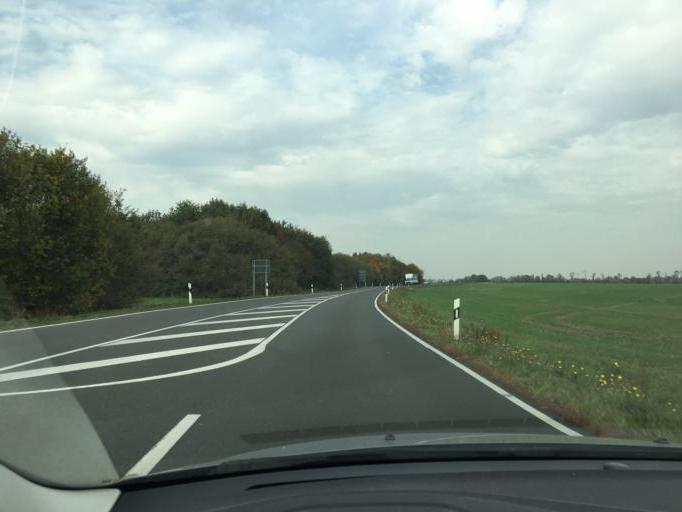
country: DE
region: Saxony
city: Zwochau
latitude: 51.4403
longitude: 12.2749
